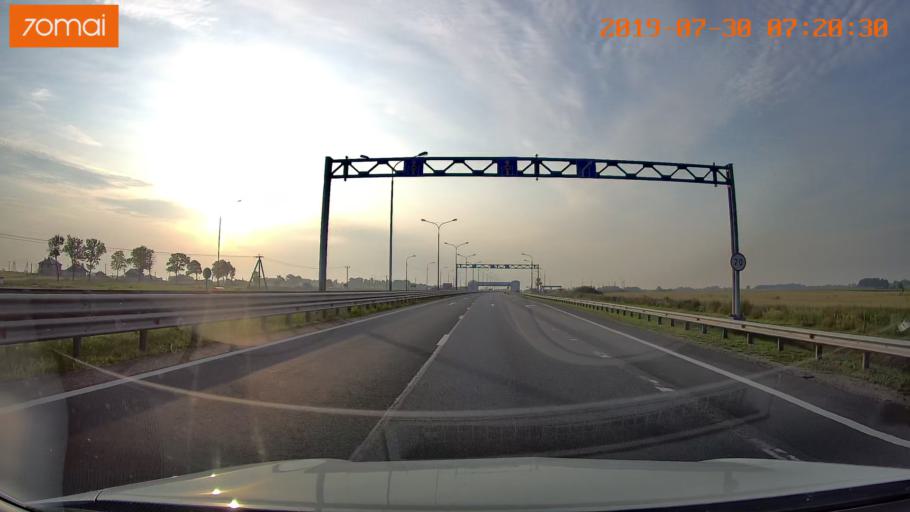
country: RU
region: Kaliningrad
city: Bol'shoe Isakovo
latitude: 54.7001
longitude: 20.7057
